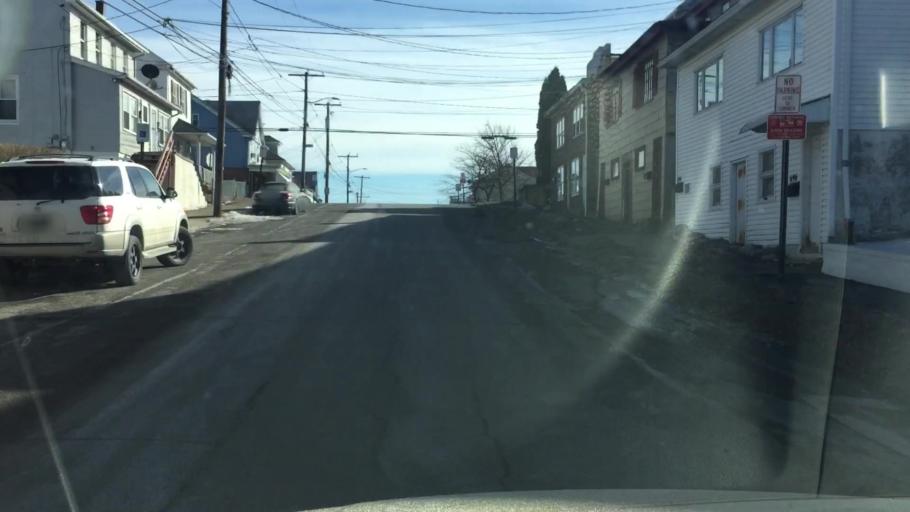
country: US
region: Pennsylvania
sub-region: Luzerne County
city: Hazleton
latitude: 40.9664
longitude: -75.9692
